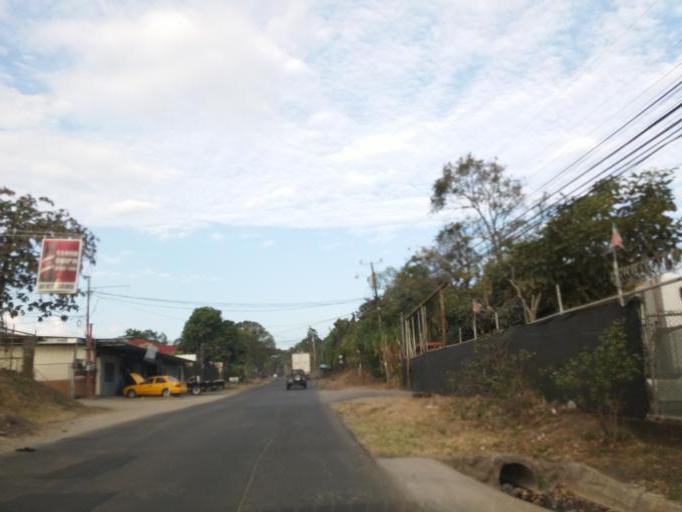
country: CR
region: Alajuela
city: Alajuela
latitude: 9.9828
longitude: -84.2240
